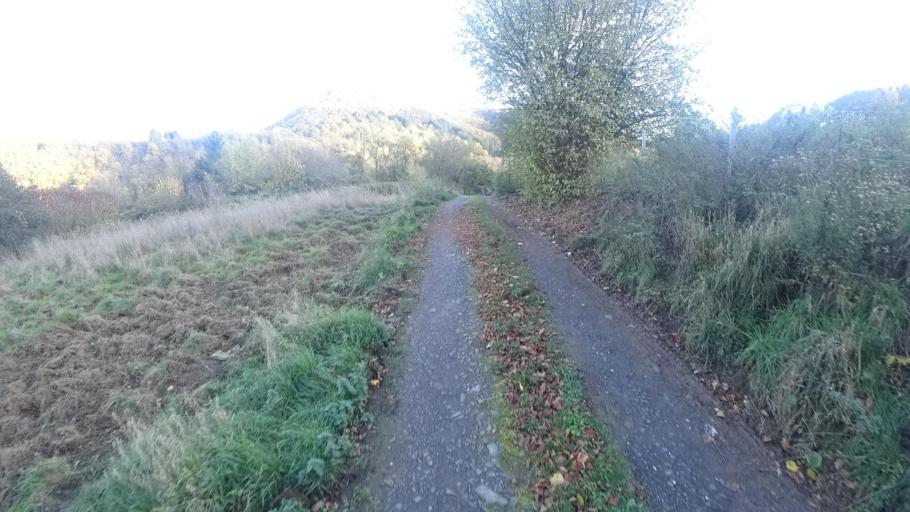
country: DE
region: Rheinland-Pfalz
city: Altenahr
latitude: 50.5069
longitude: 6.9762
